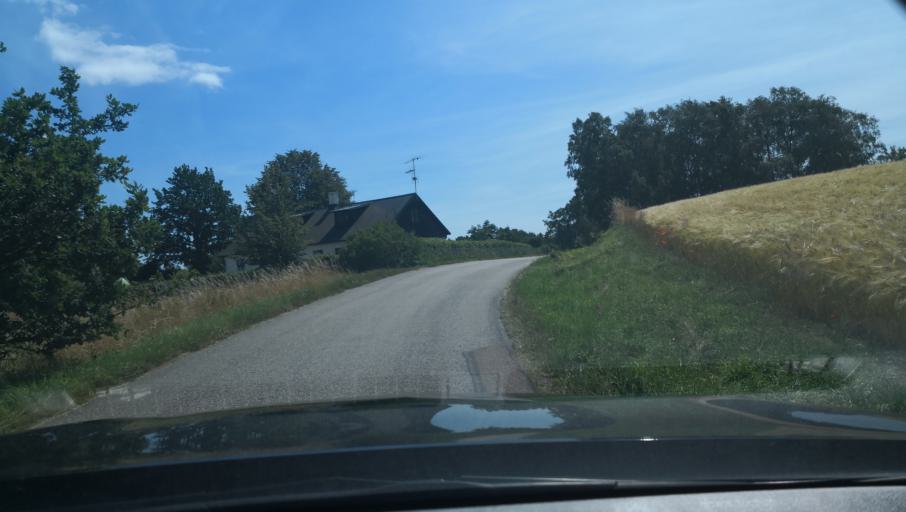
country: SE
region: Skane
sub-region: Ystads Kommun
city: Kopingebro
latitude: 55.3902
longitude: 14.1415
